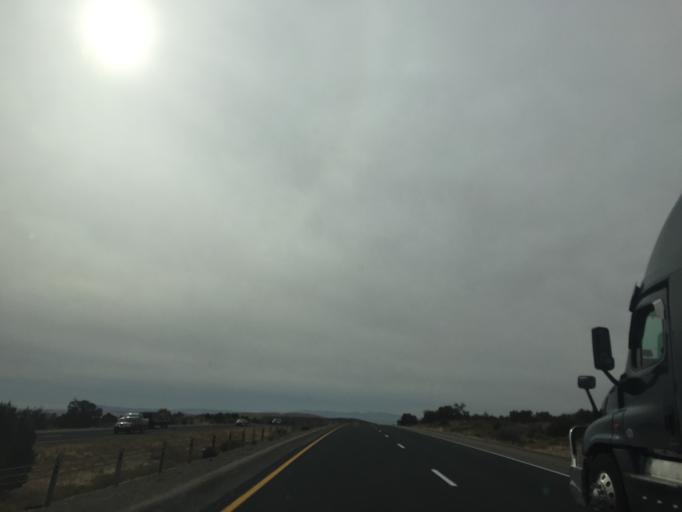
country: US
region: Utah
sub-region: Washington County
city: Toquerville
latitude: 37.2611
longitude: -113.3290
